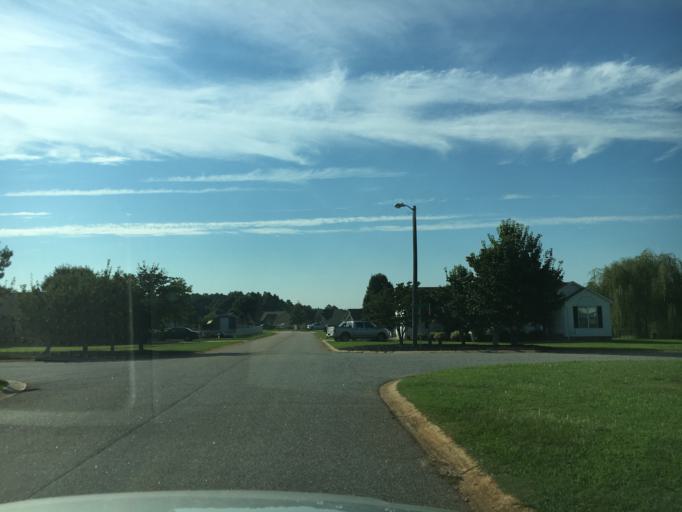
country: US
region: South Carolina
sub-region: Spartanburg County
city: Boiling Springs
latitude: 35.0862
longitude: -81.9363
